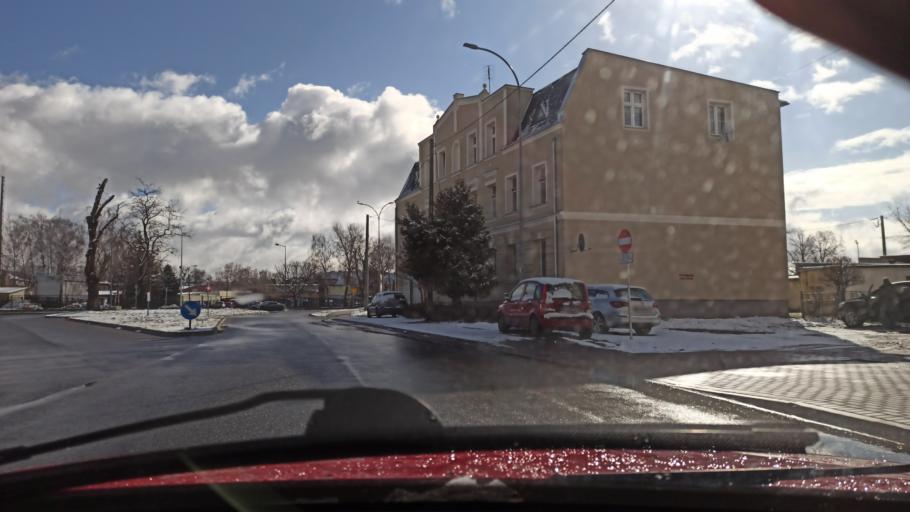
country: PL
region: Warmian-Masurian Voivodeship
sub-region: Powiat elblaski
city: Elblag
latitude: 54.1531
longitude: 19.3957
